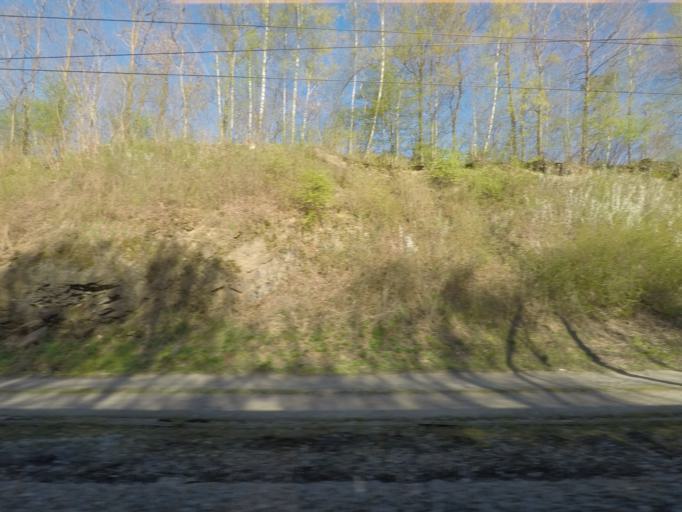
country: BE
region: Wallonia
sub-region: Province du Luxembourg
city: Tellin
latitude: 50.0869
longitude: 5.2767
